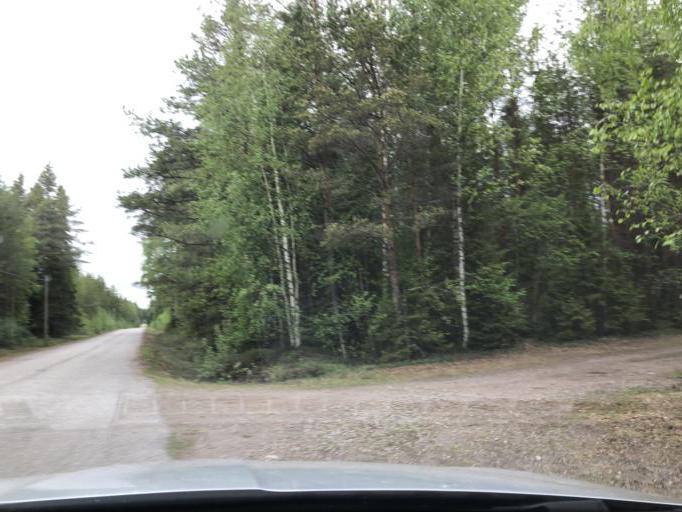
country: SE
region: Norrbotten
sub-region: Pitea Kommun
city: Roknas
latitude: 65.3803
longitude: 21.2742
